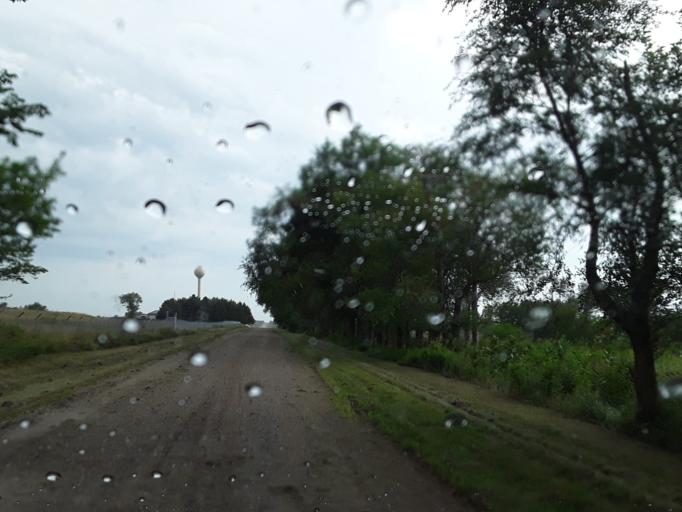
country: US
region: Nebraska
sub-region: Saunders County
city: Yutan
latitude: 41.1911
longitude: -96.4449
